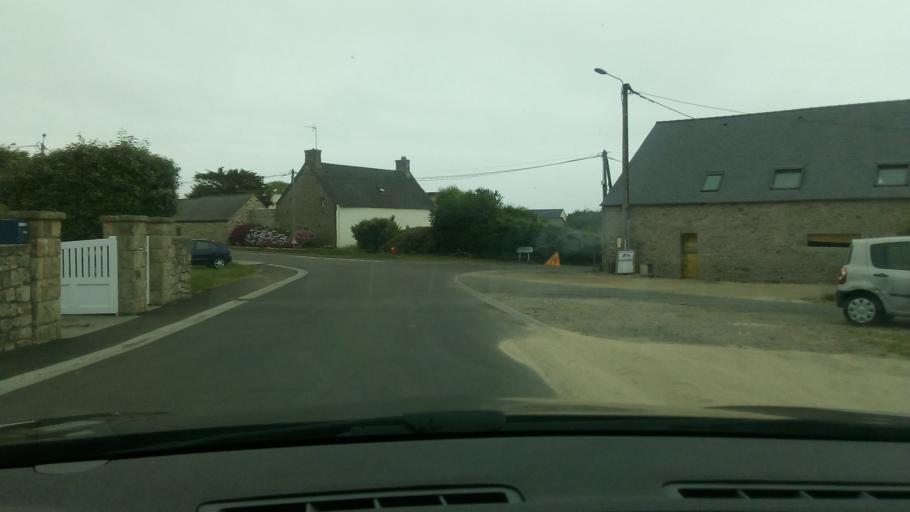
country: FR
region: Brittany
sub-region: Departement du Finistere
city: Le Conquet
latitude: 48.3529
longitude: -4.7712
